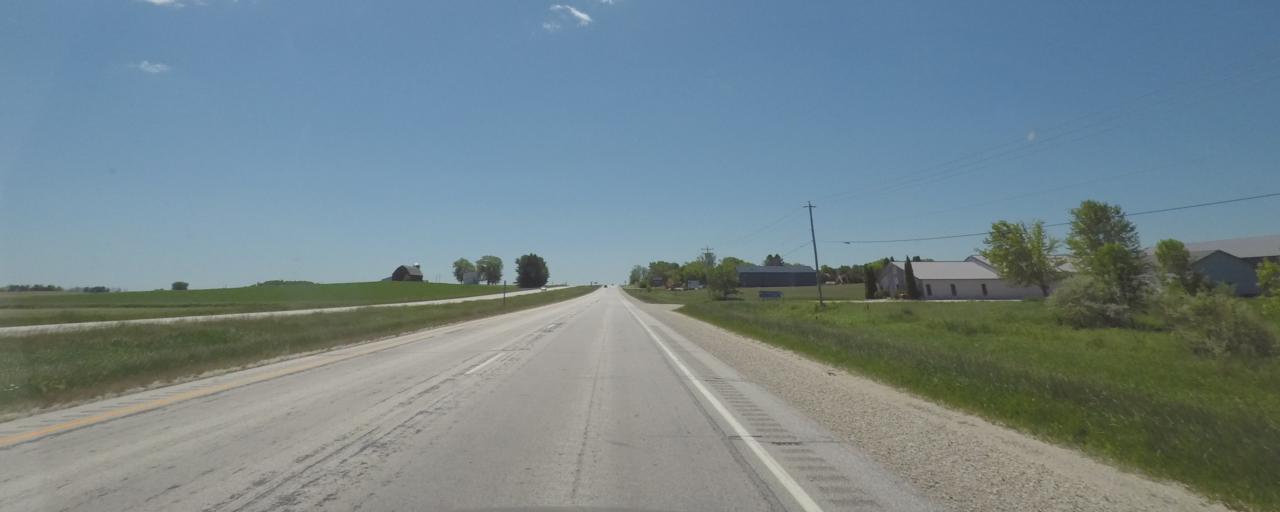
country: US
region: Wisconsin
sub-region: Sheboygan County
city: Plymouth
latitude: 43.6940
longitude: -87.9409
